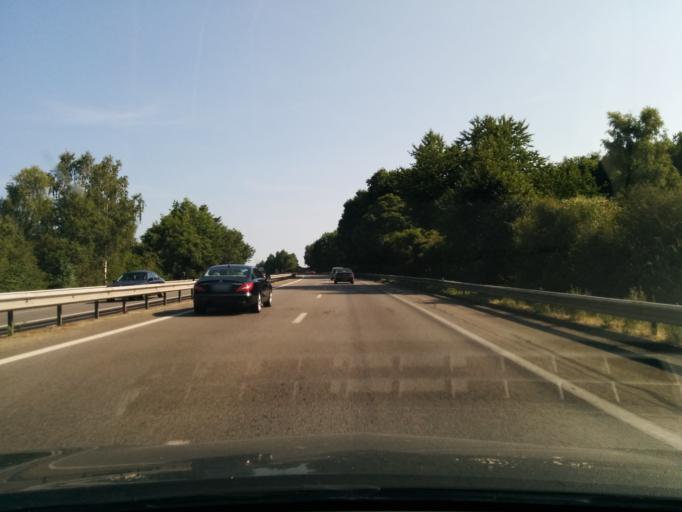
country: FR
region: Limousin
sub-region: Departement de la Haute-Vienne
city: Condat-sur-Vienne
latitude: 45.7860
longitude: 1.3029
